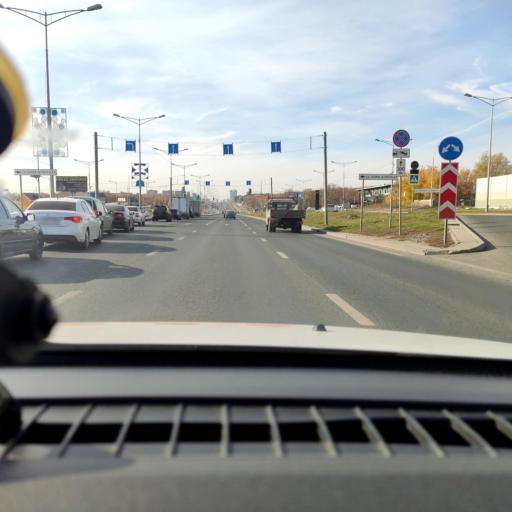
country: RU
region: Samara
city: Petra-Dubrava
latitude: 53.2719
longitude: 50.2588
